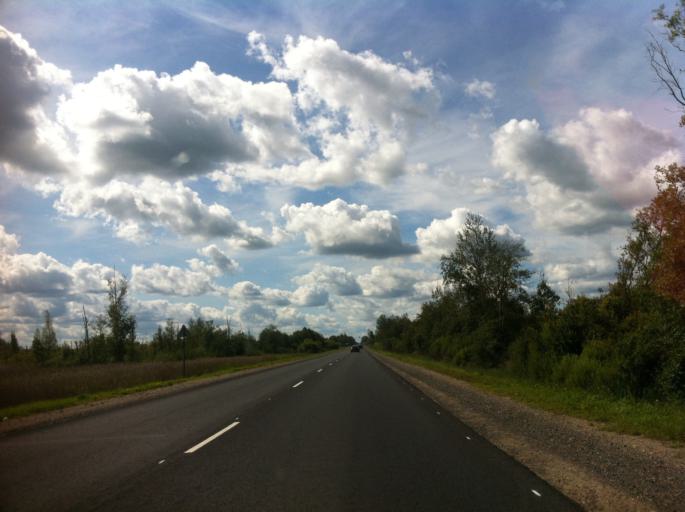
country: RU
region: Pskov
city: Izborsk
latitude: 57.7422
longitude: 28.0171
